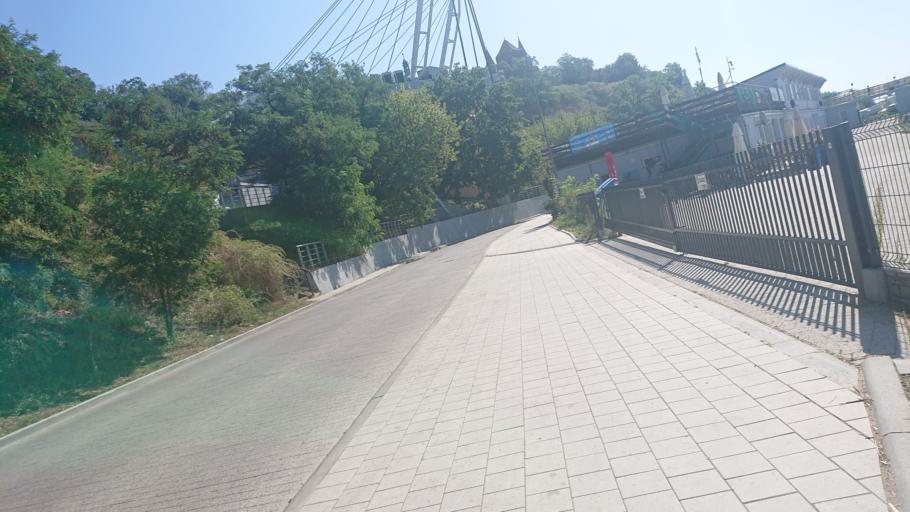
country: PL
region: Masovian Voivodeship
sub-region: Plock
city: Plock
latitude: 52.5419
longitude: 19.6849
